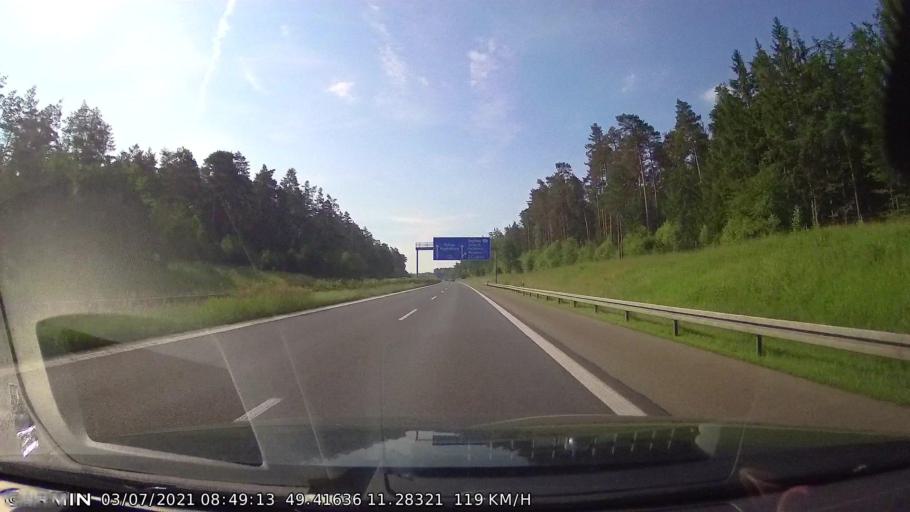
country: DE
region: Bavaria
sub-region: Regierungsbezirk Mittelfranken
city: Winkelhaid
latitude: 49.4162
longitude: 11.2834
